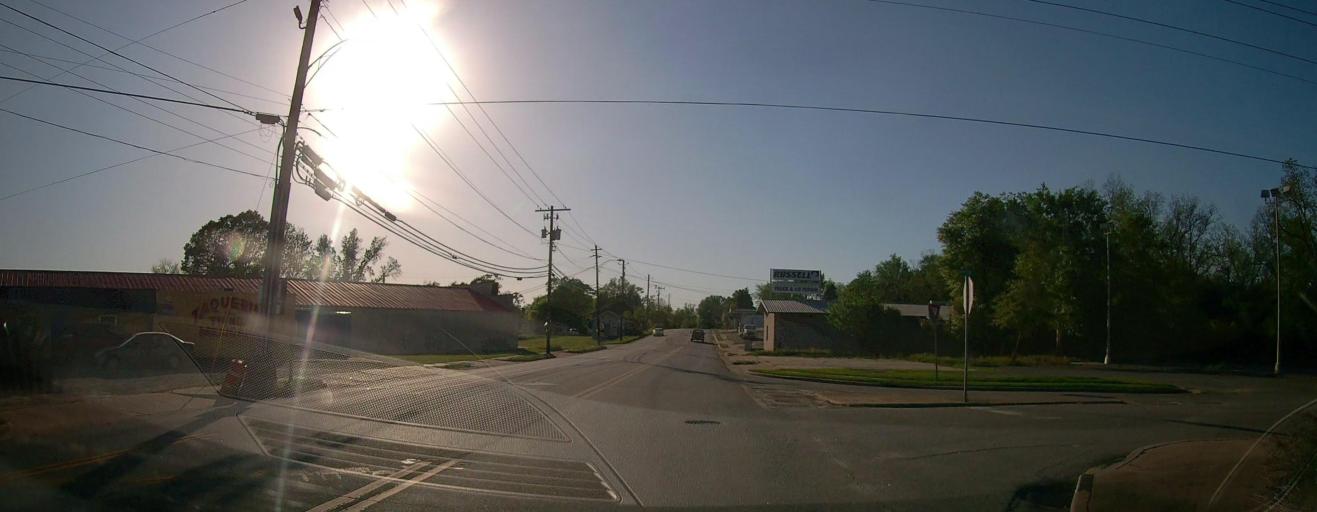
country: US
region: Georgia
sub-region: Macon County
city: Montezuma
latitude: 32.3005
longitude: -84.0309
